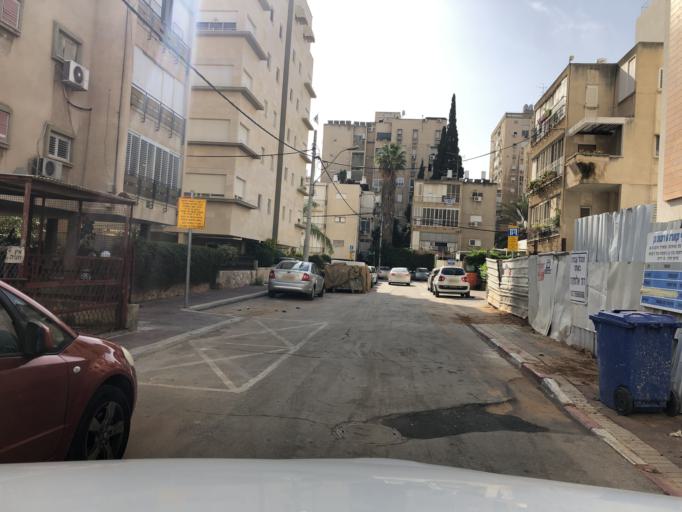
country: IL
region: Tel Aviv
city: Bene Beraq
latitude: 32.0681
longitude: 34.8293
